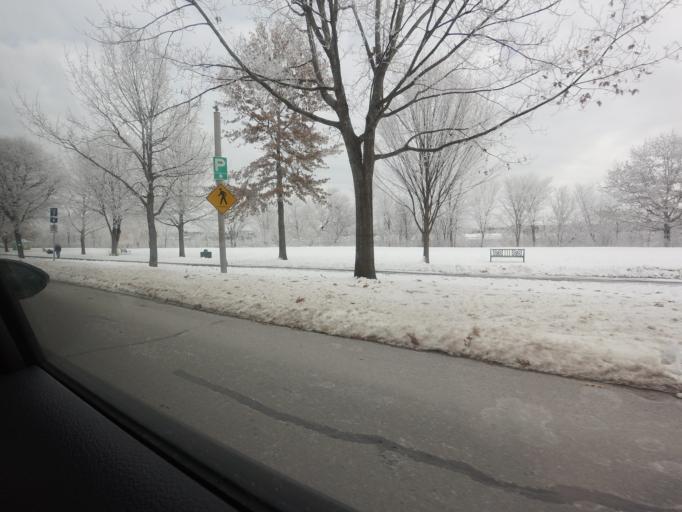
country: CA
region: New Brunswick
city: Fredericton
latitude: 45.9578
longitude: -66.6341
